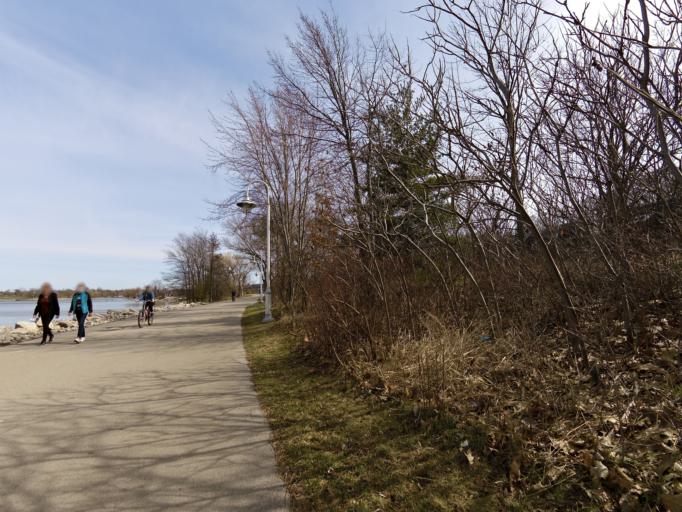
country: CA
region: Ontario
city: Hamilton
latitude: 43.2718
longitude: -79.8838
